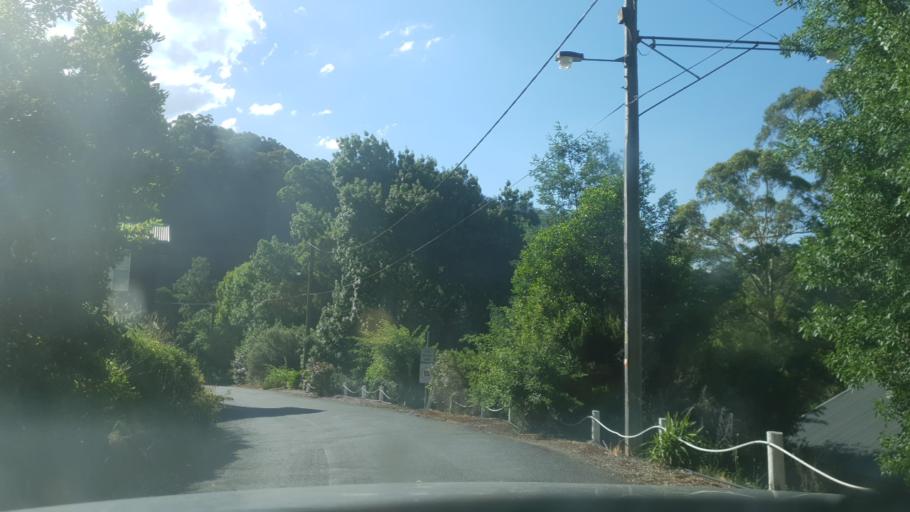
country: AU
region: Victoria
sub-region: Alpine
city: Mount Beauty
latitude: -36.8038
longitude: 147.2258
